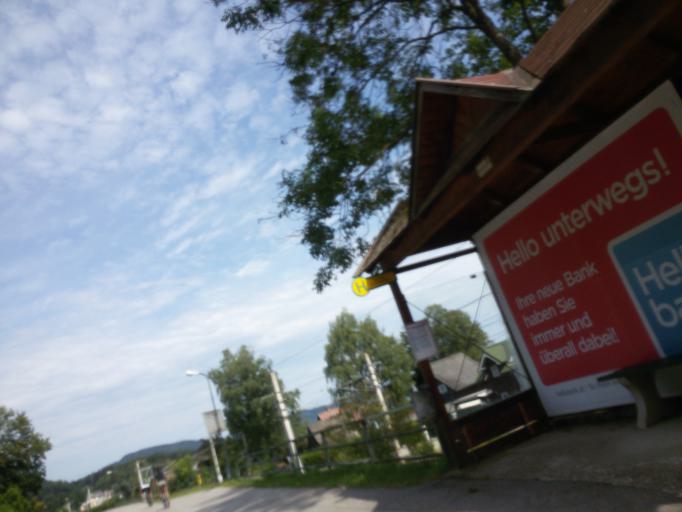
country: AT
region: Carinthia
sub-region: Politischer Bezirk Klagenfurt Land
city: Schiefling am See
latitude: 46.6312
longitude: 14.1029
